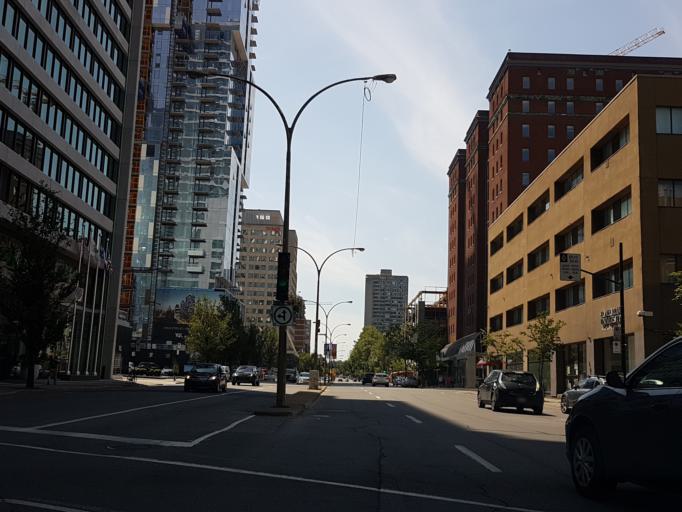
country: CA
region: Quebec
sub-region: Montreal
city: Montreal
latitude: 45.4958
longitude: -73.5733
